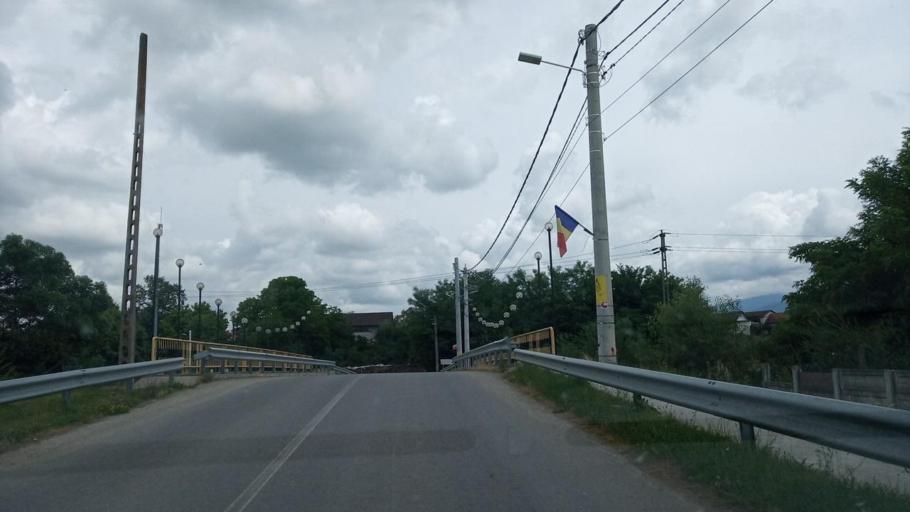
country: RO
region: Sibiu
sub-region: Comuna Cartisoara
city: Cartisoara
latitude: 45.7282
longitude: 24.5779
